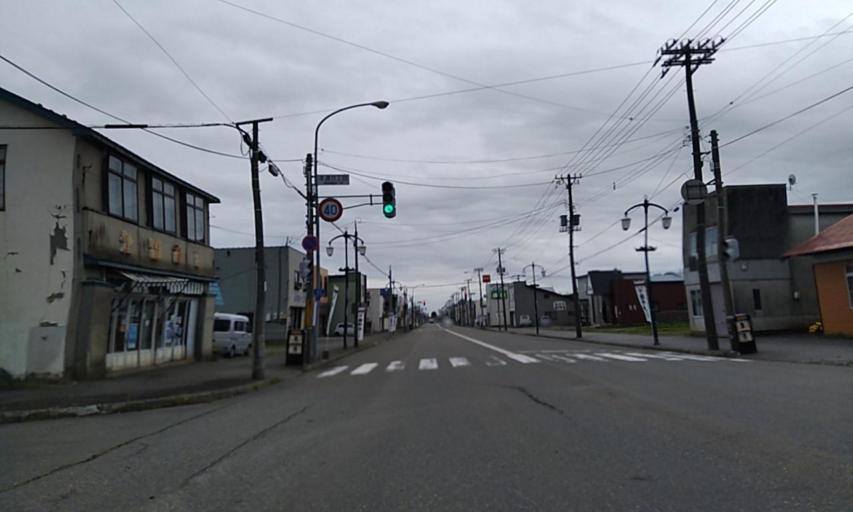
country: JP
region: Hokkaido
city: Obihiro
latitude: 42.2914
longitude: 143.3134
